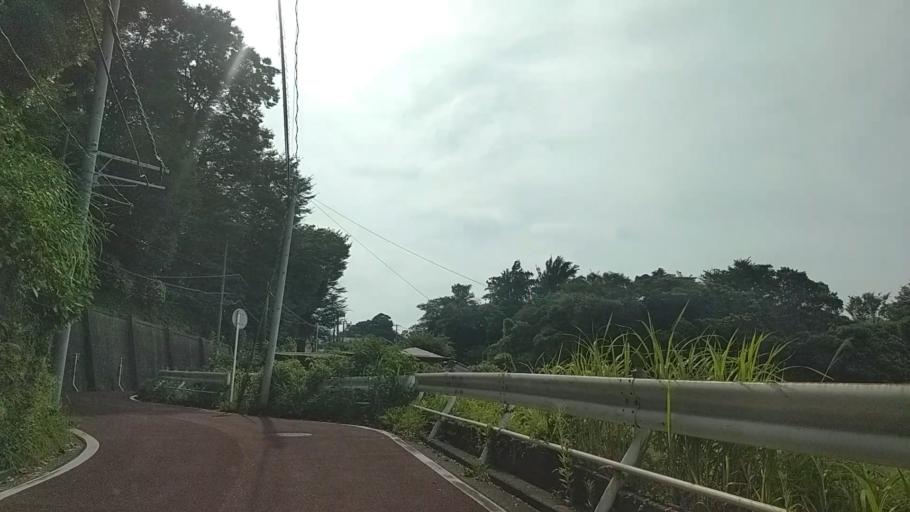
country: JP
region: Kanagawa
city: Yokohama
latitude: 35.4328
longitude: 139.6625
